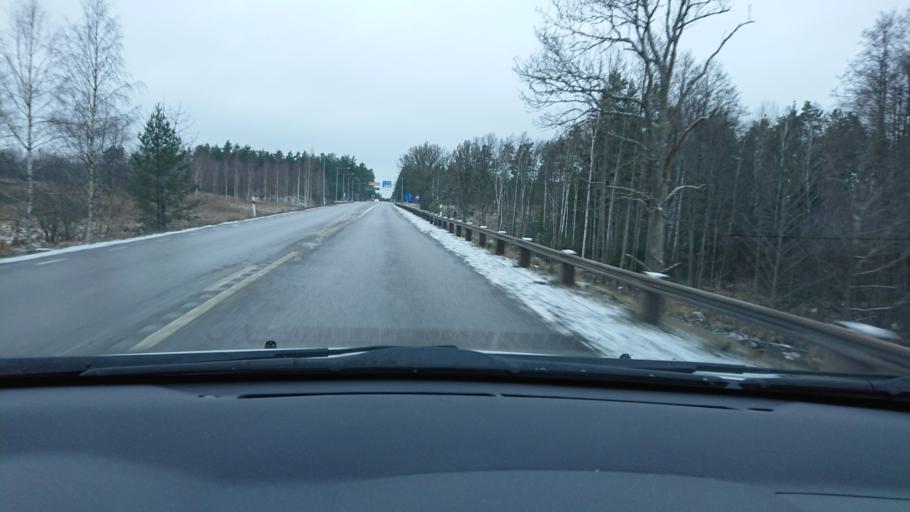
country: SE
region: Kalmar
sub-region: Hultsfreds Kommun
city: Hultsfred
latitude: 57.4867
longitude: 15.8284
